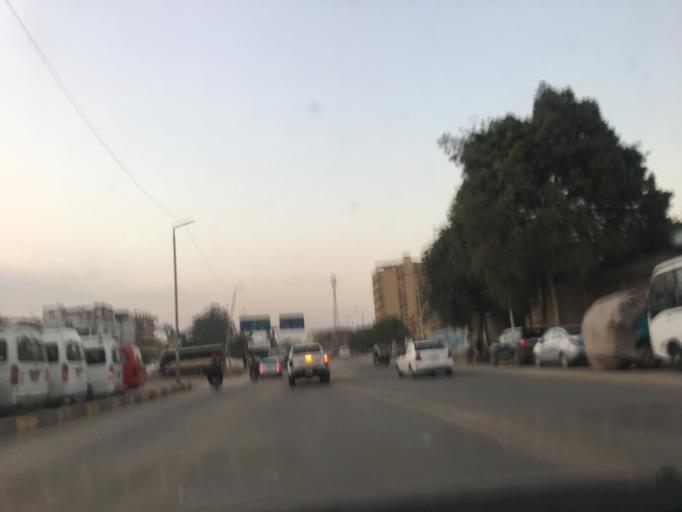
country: EG
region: Al Jizah
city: Al Jizah
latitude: 29.9917
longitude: 31.1305
